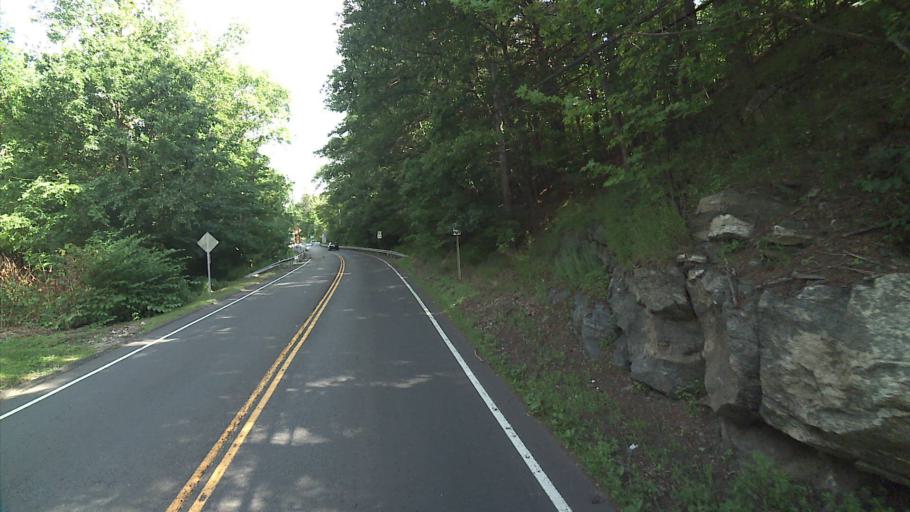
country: US
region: Connecticut
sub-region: New Haven County
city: Middlebury
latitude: 41.5390
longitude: -73.0881
